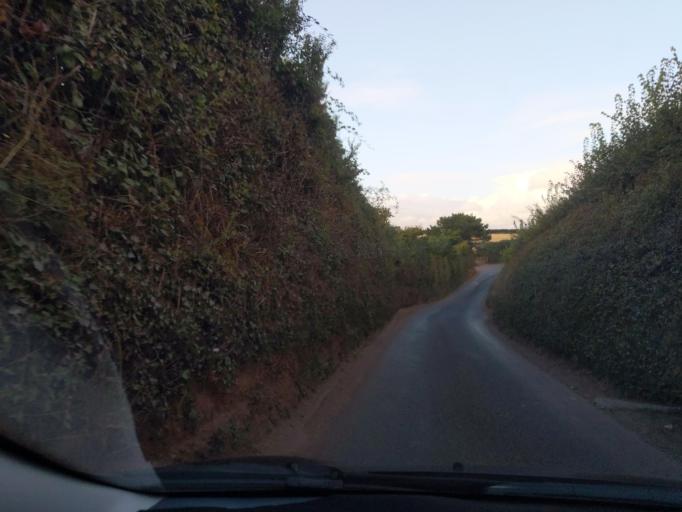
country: GB
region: England
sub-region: Devon
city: Salcombe
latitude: 50.2418
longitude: -3.8212
